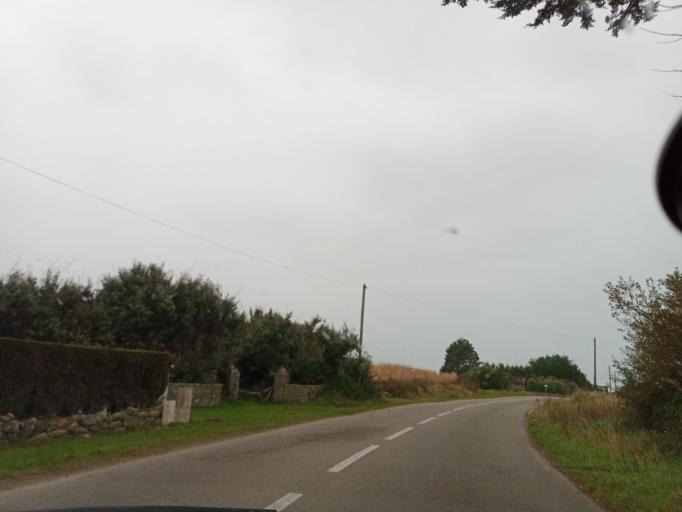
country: FR
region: Brittany
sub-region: Departement du Finistere
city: Esquibien
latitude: 48.0189
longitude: -4.5587
